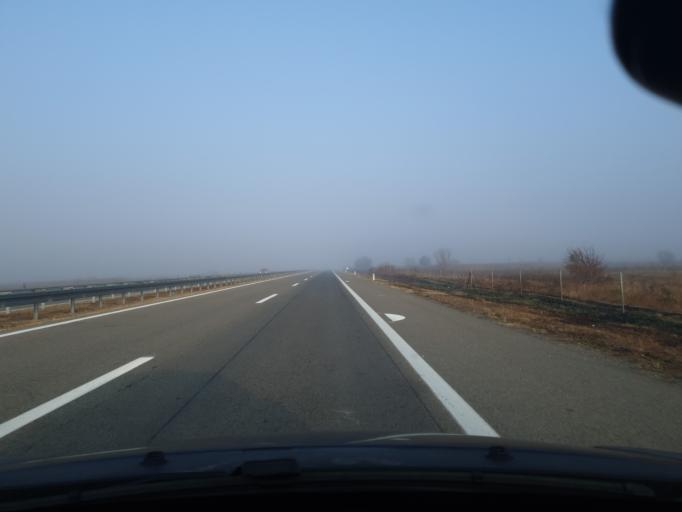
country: RS
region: Central Serbia
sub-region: Jablanicki Okrug
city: Leskovac
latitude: 43.0747
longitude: 21.9569
